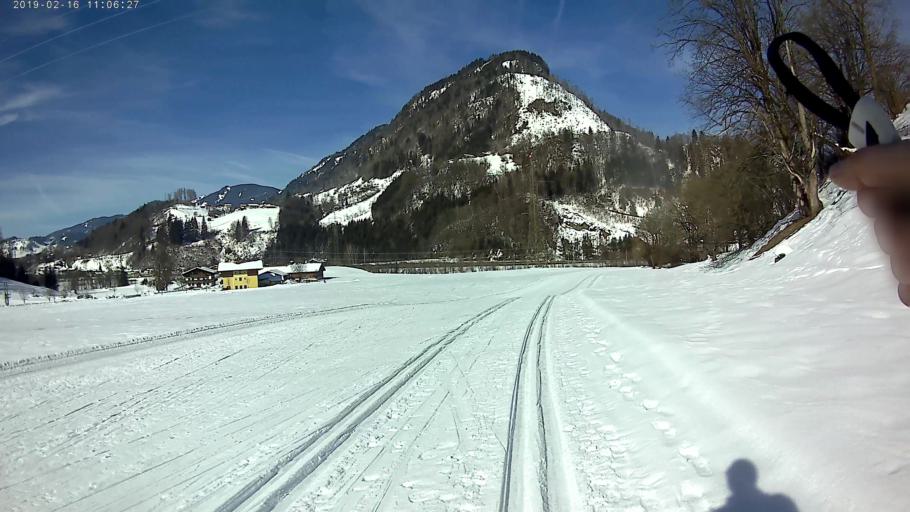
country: AT
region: Salzburg
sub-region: Politischer Bezirk Sankt Johann im Pongau
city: Sankt Johann im Pongau
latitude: 47.3260
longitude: 13.1875
